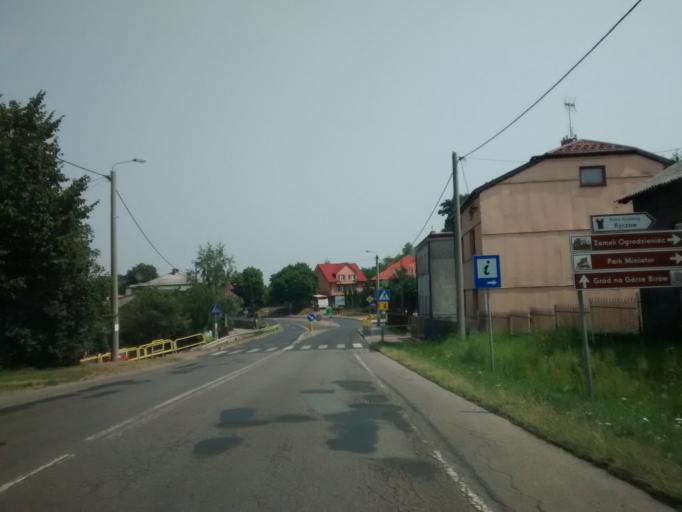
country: PL
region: Silesian Voivodeship
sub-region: Powiat zawiercianski
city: Ogrodzieniec
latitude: 50.4544
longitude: 19.5466
